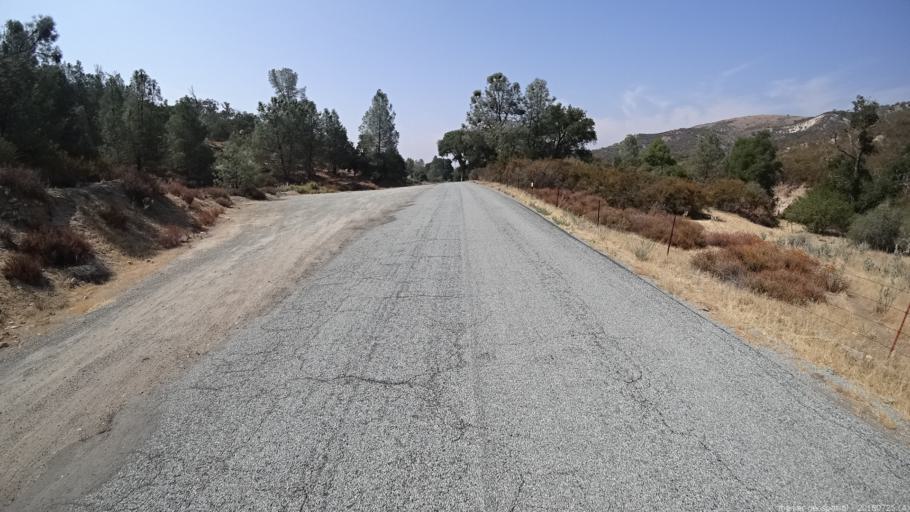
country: US
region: California
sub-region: San Luis Obispo County
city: San Miguel
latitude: 35.9008
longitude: -120.5523
